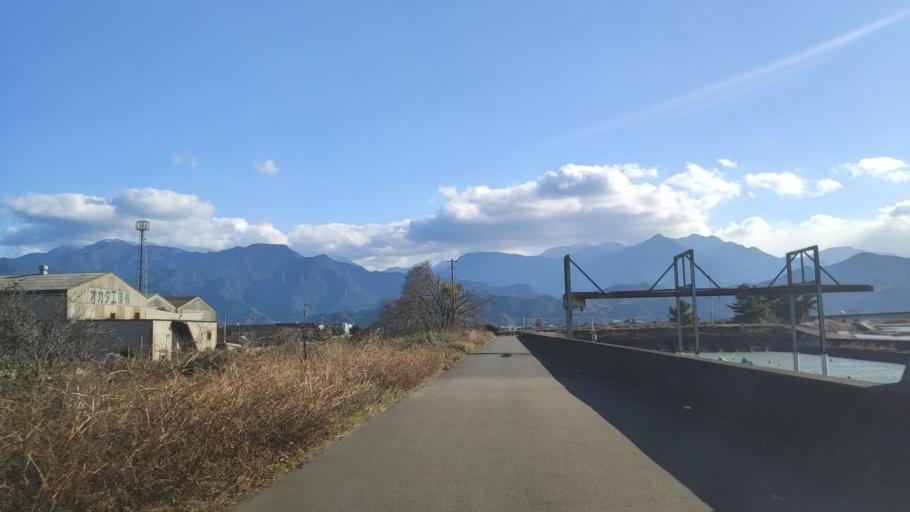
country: JP
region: Ehime
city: Saijo
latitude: 33.9219
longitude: 133.1559
